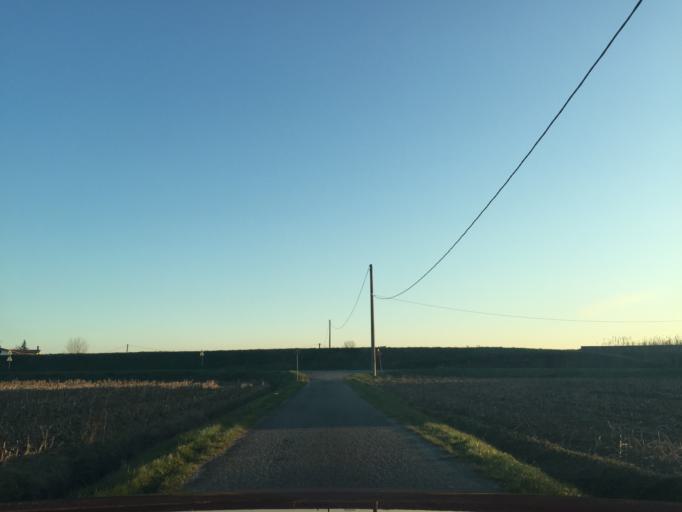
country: IT
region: Tuscany
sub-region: Provincia di Pistoia
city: Anchione
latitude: 43.8370
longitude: 10.7583
